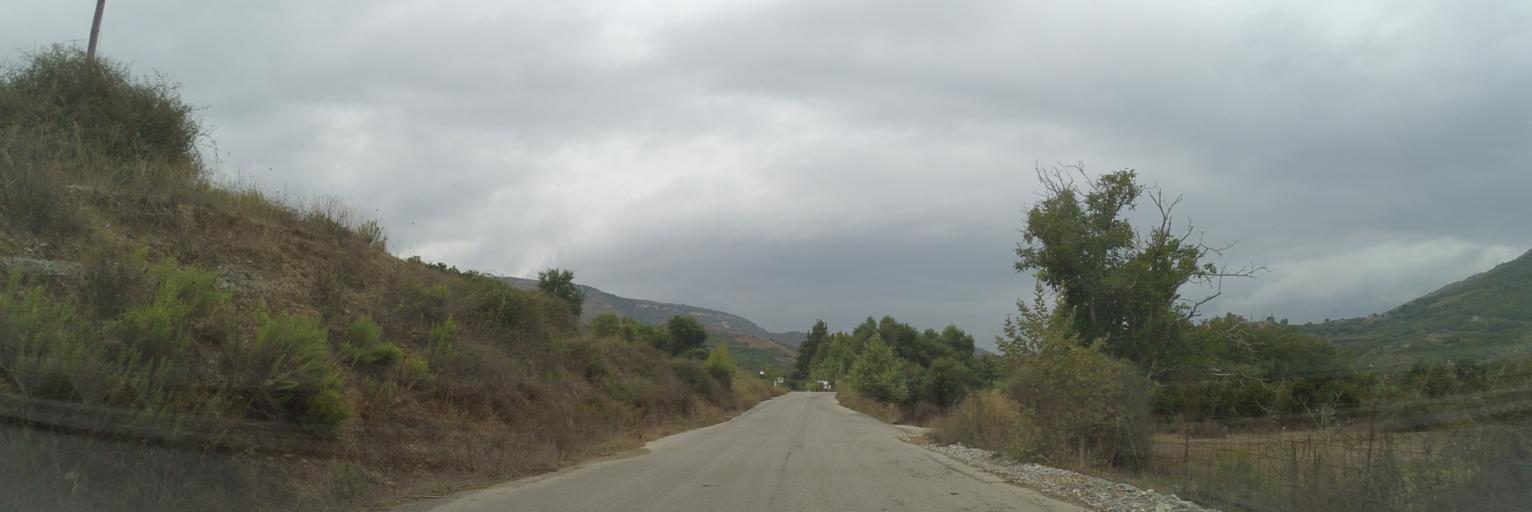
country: GR
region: Crete
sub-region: Nomos Rethymnis
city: Agia Foteini
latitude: 35.2884
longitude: 24.5632
